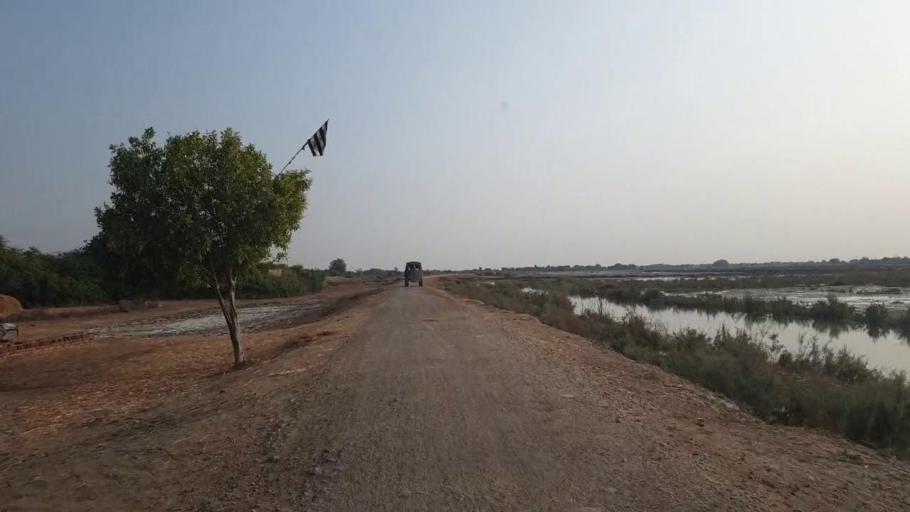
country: PK
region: Sindh
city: Rajo Khanani
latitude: 25.0478
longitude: 68.7659
